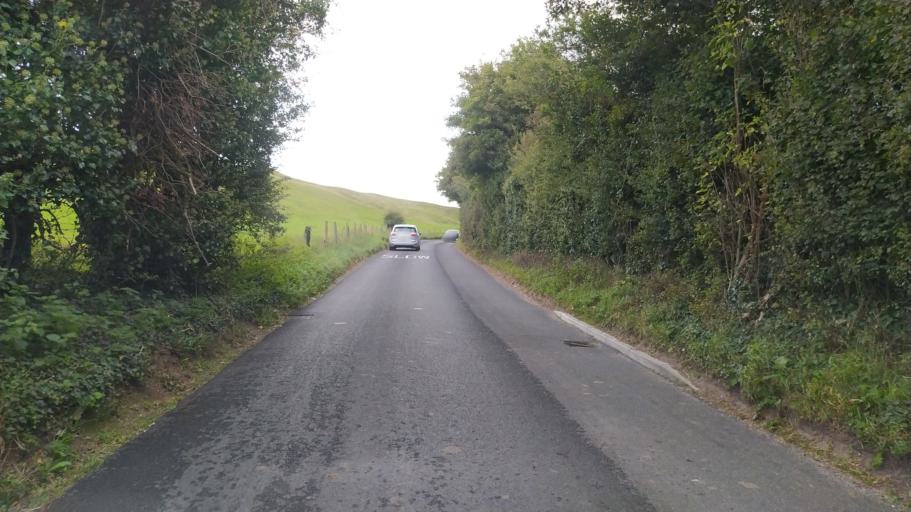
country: GB
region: England
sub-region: Dorset
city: Overcombe
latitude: 50.6604
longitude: -2.4289
